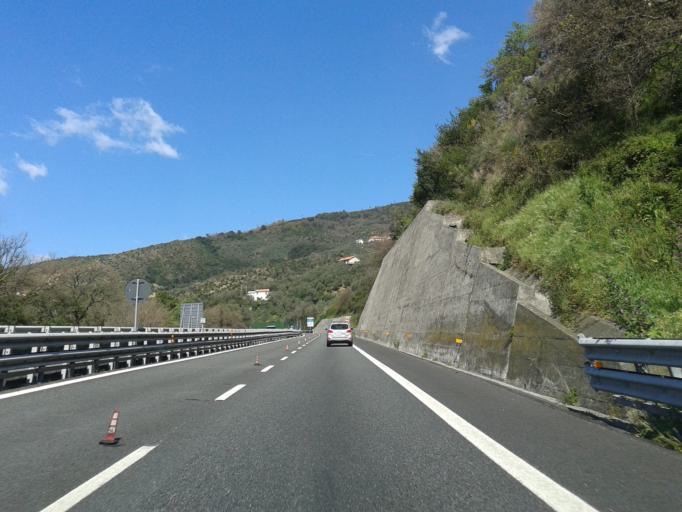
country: IT
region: Liguria
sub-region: Provincia di Genova
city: Sestri Levante
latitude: 44.2817
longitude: 9.4107
